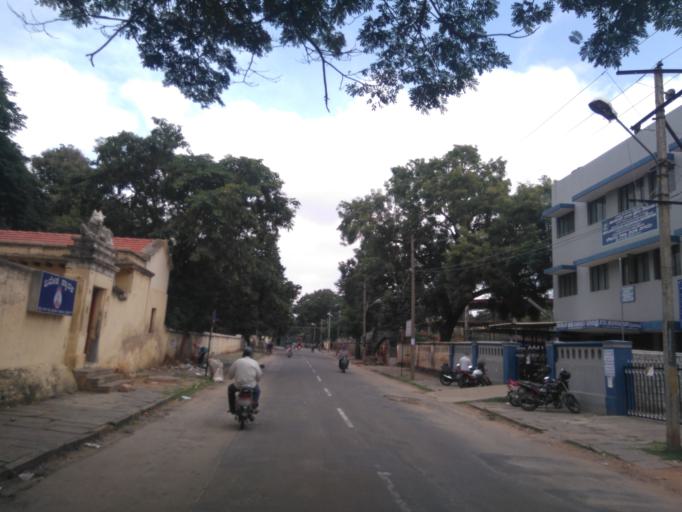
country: IN
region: Karnataka
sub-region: Mysore
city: Mysore
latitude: 12.3077
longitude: 76.6474
